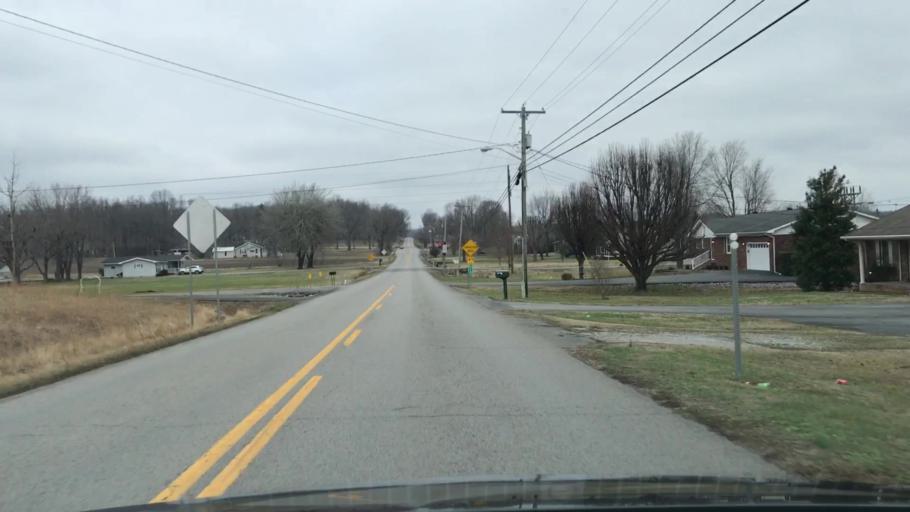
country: US
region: Kentucky
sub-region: Muhlenberg County
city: Greenville
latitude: 37.2206
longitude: -87.1939
